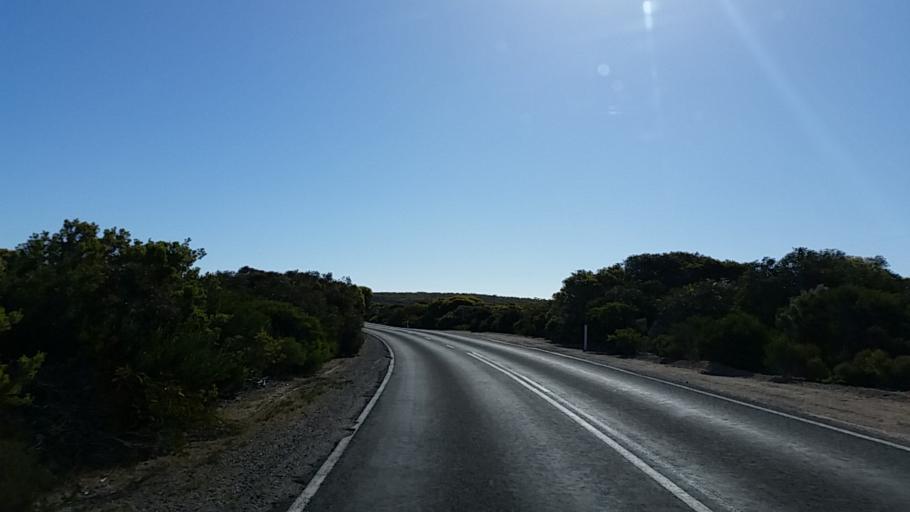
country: AU
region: South Australia
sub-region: Yorke Peninsula
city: Honiton
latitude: -35.2668
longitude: 136.9438
